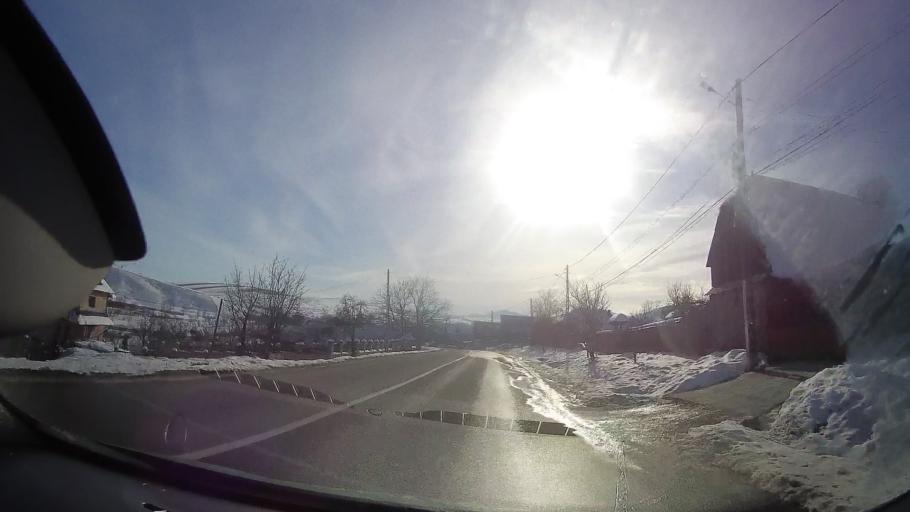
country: RO
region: Neamt
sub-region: Comuna Baltatesti
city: Valea Seaca
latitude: 47.1358
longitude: 26.3140
